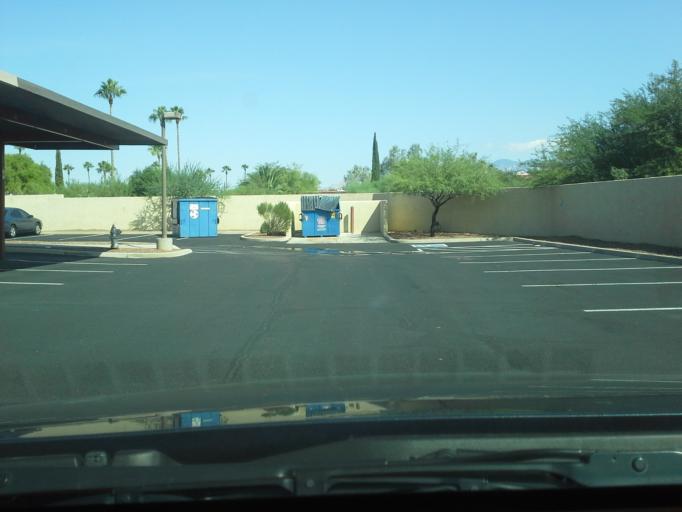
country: US
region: Arizona
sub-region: Pima County
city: South Tucson
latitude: 32.2193
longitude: -111.0252
